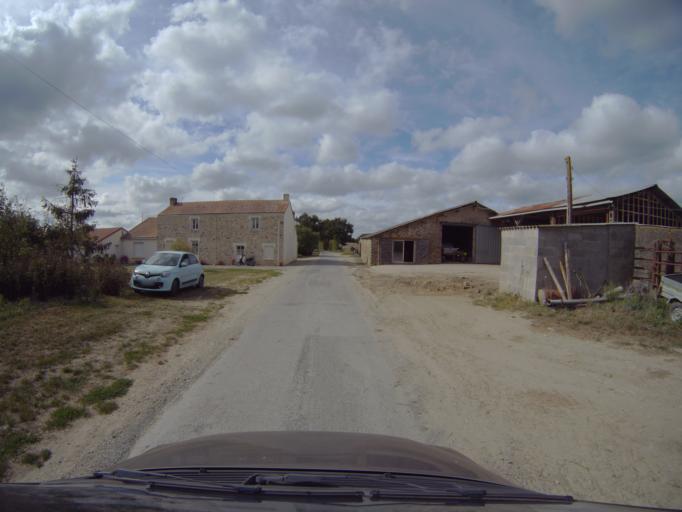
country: FR
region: Pays de la Loire
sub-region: Departement de la Loire-Atlantique
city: La Planche
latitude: 47.0263
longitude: -1.4106
